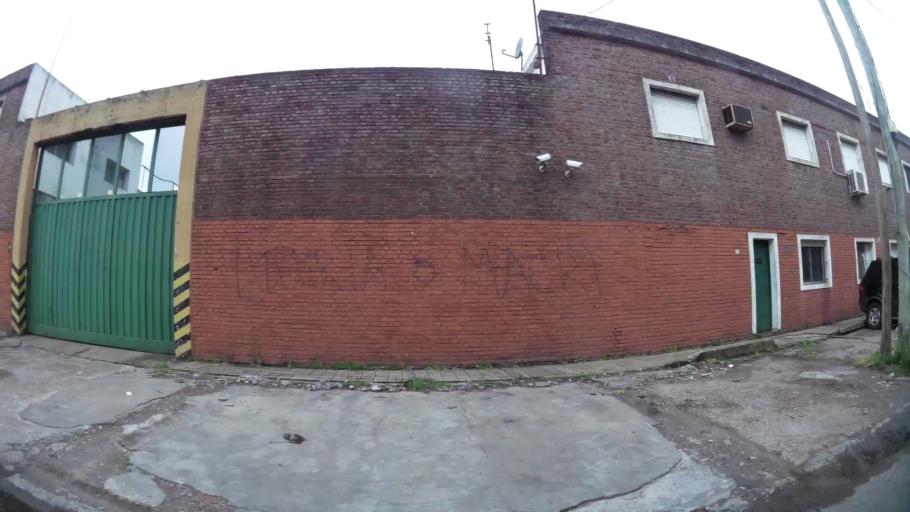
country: AR
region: Buenos Aires
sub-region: Partido de Lanus
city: Lanus
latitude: -34.7132
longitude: -58.3602
